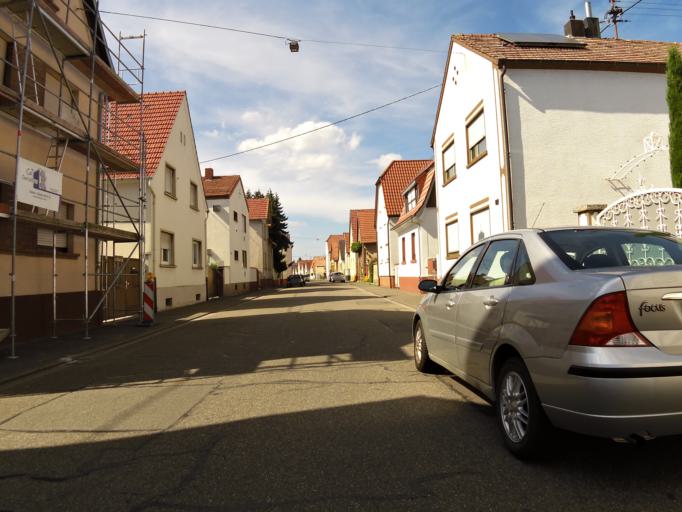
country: DE
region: Rheinland-Pfalz
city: Bohl-Iggelheim
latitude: 49.3584
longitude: 8.3144
